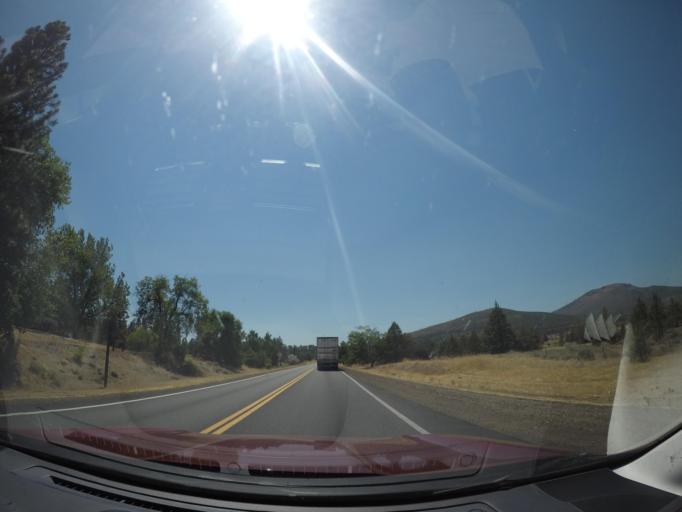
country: US
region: California
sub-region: Shasta County
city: Burney
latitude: 41.0003
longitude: -121.4491
